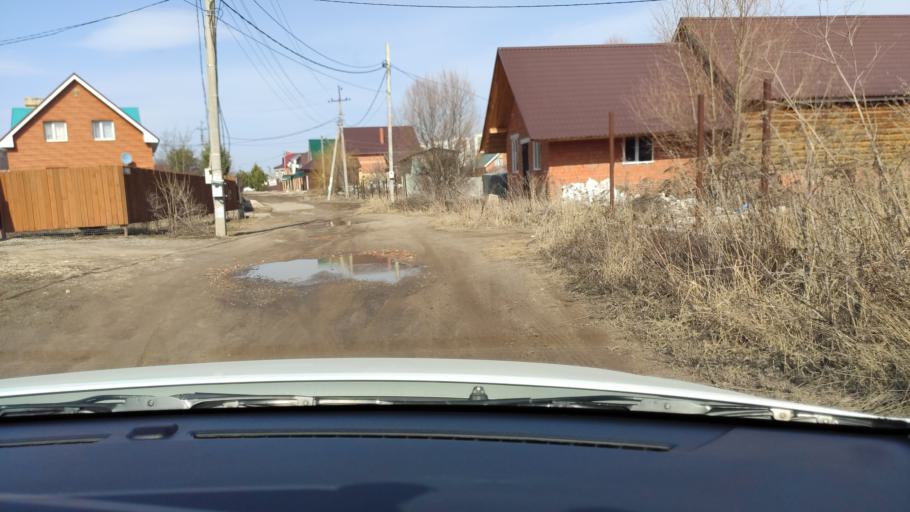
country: RU
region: Tatarstan
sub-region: Gorod Kazan'
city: Kazan
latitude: 55.7845
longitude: 49.2482
